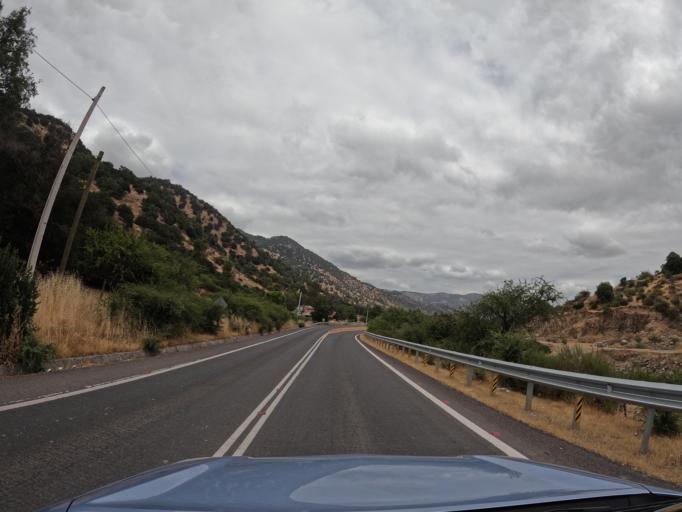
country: CL
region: Maule
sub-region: Provincia de Curico
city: Teno
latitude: -34.8187
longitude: -71.2093
